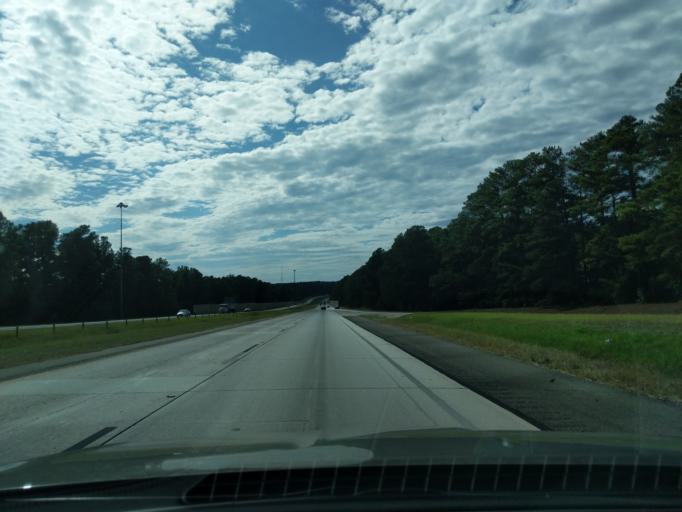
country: US
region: Georgia
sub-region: Columbia County
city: Evans
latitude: 33.4818
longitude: -82.1349
